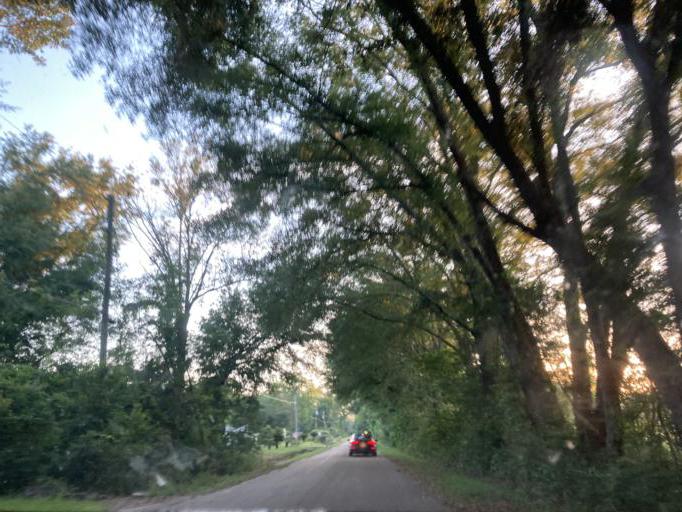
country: US
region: Florida
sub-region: Jackson County
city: Graceville
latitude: 30.9455
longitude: -85.3899
